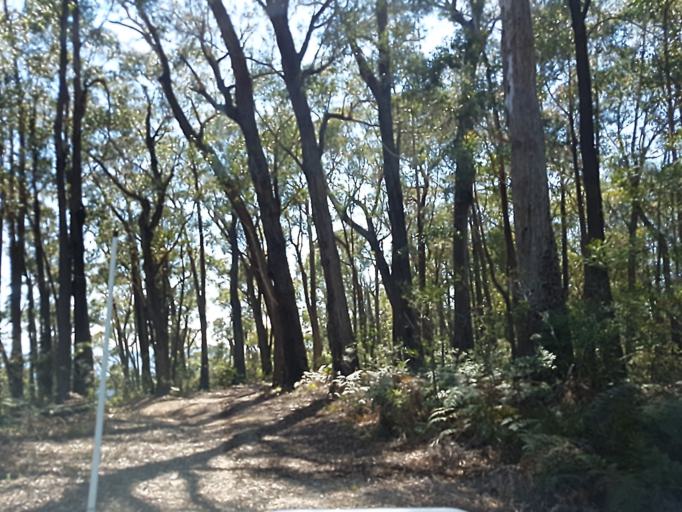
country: AU
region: Victoria
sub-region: East Gippsland
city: Lakes Entrance
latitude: -37.2902
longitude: 148.3221
